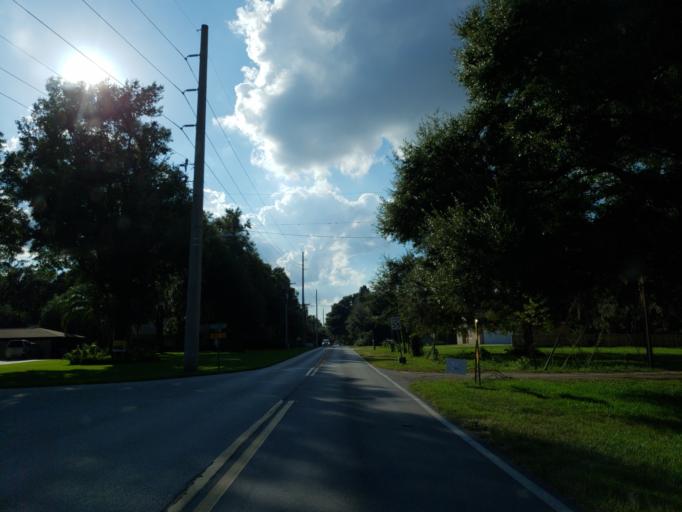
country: US
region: Florida
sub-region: Hillsborough County
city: Bloomingdale
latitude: 27.8938
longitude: -82.2155
